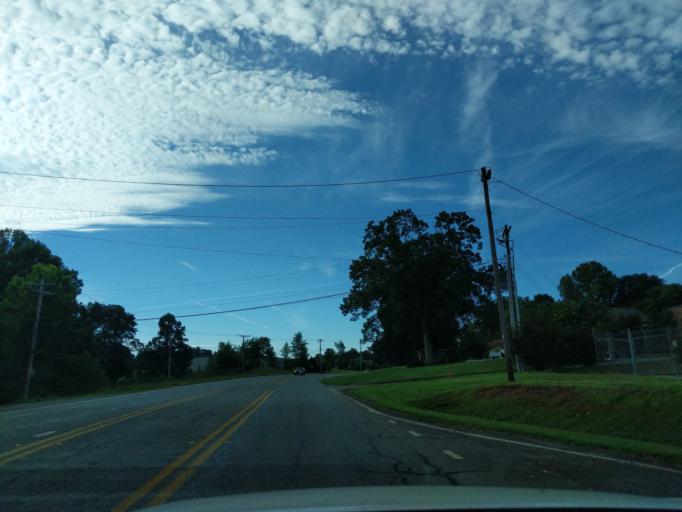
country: US
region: Georgia
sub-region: Fannin County
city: McCaysville
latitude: 34.9588
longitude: -84.3682
